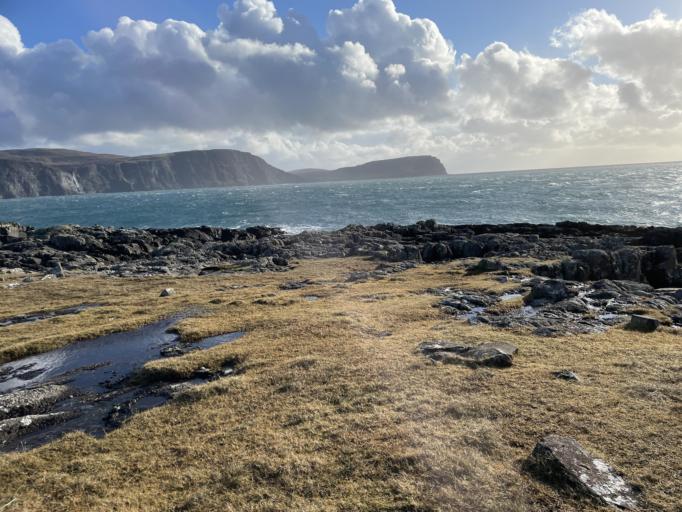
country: GB
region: Scotland
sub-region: Eilean Siar
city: Harris
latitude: 57.4208
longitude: -6.7854
